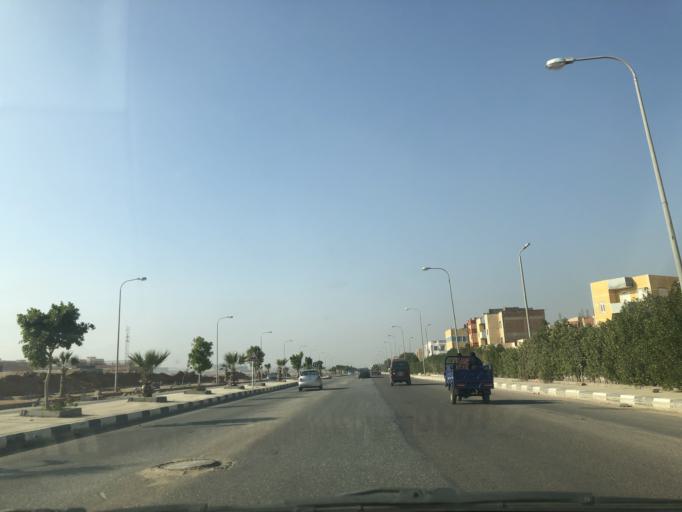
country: EG
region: Al Jizah
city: Madinat Sittah Uktubar
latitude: 29.9276
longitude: 31.0507
